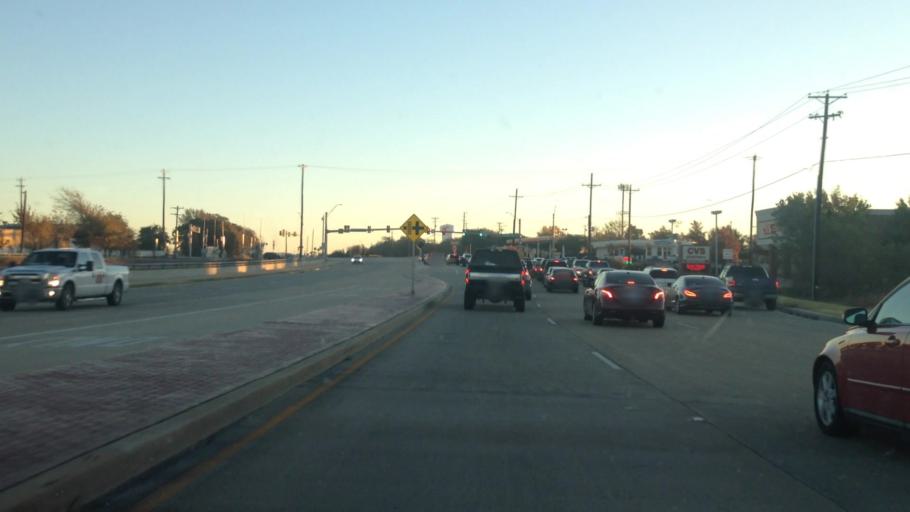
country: US
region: Texas
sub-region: Tarrant County
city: Southlake
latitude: 32.9141
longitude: -97.1281
